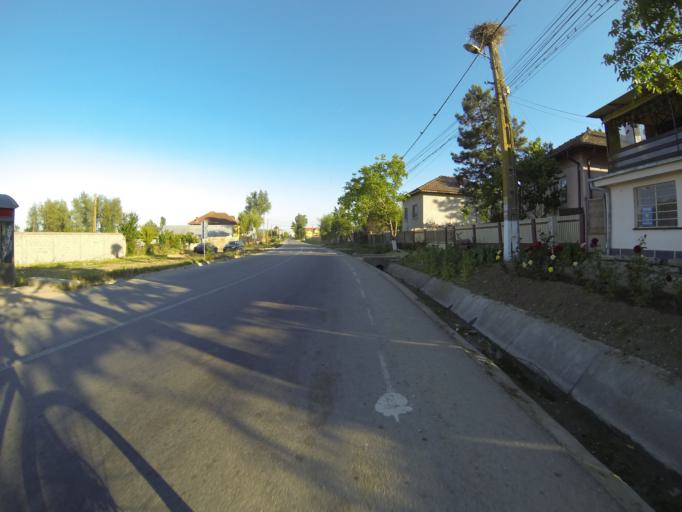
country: RO
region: Dolj
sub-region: Comuna Podari
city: Podari
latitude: 44.2252
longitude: 23.7889
